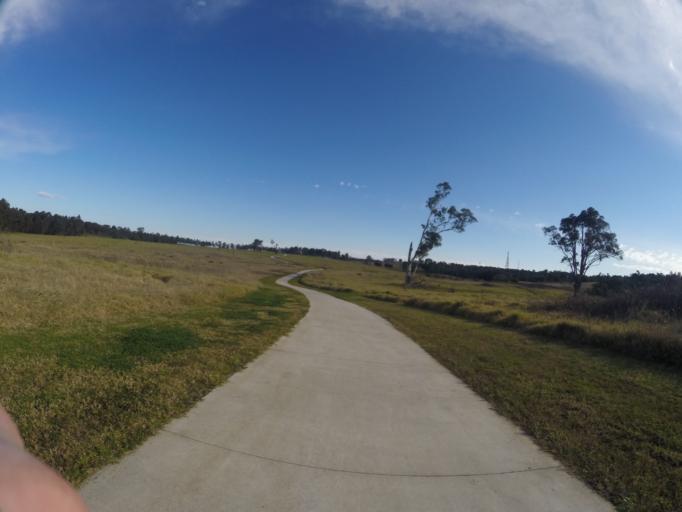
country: AU
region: New South Wales
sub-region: Fairfield
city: Horsley Park
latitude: -33.8576
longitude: 150.8714
